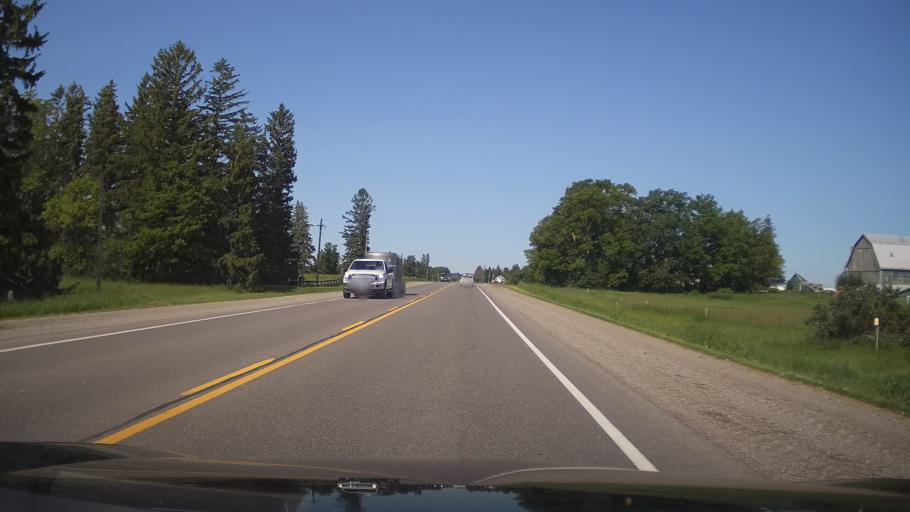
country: CA
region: Ontario
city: Omemee
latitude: 44.3436
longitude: -78.8323
